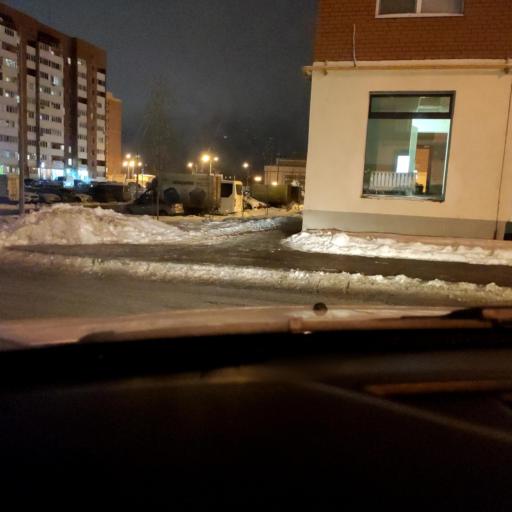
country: RU
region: Samara
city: Petra-Dubrava
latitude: 53.3078
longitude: 50.2872
